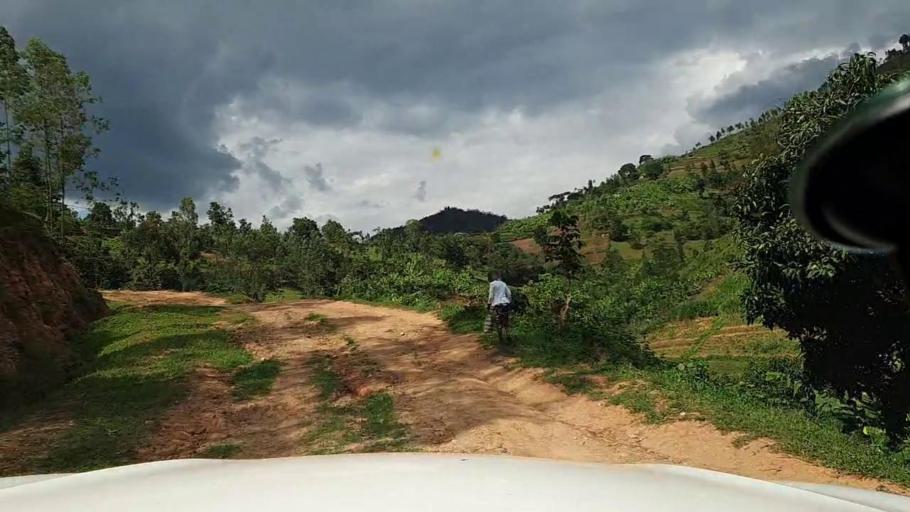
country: RW
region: Southern Province
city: Gitarama
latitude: -1.8216
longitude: 29.8013
